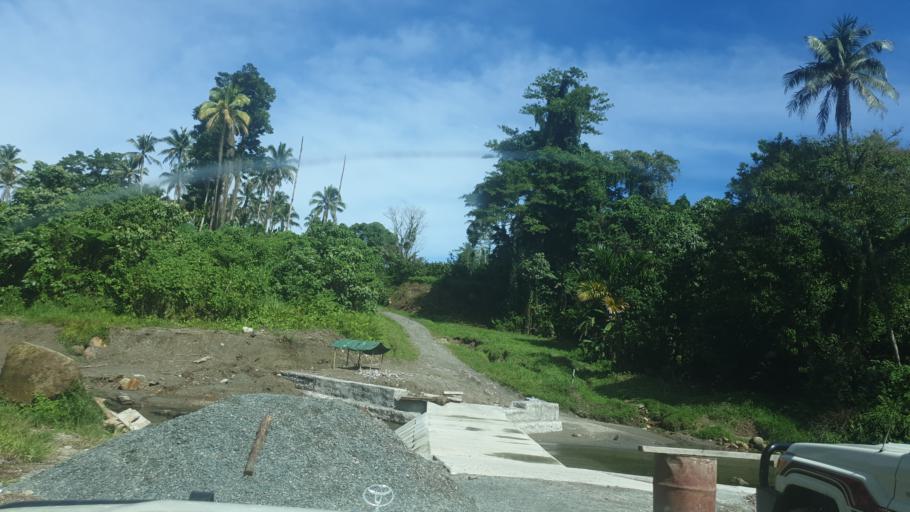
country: PG
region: Bougainville
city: Panguna
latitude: -6.5027
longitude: 155.3278
